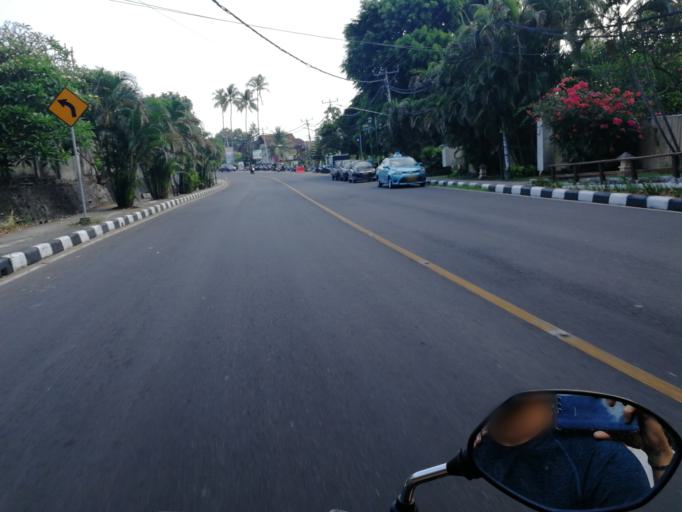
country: ID
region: West Nusa Tenggara
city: Mambalan
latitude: -8.4949
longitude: 116.0448
